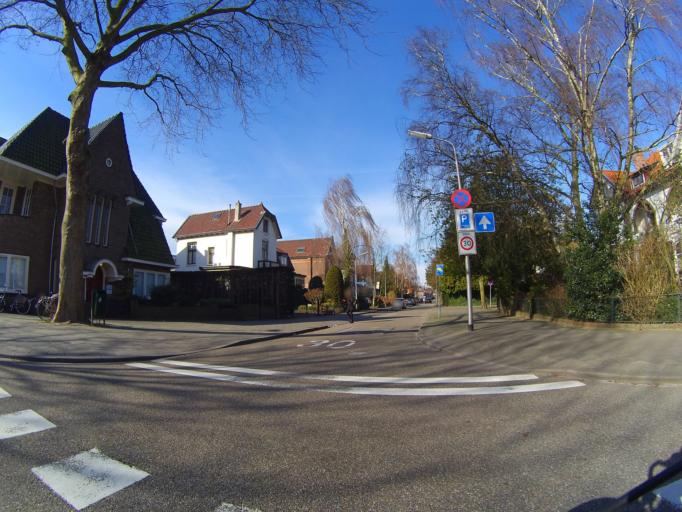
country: NL
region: North Holland
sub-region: Gemeente Bussum
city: Bussum
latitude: 52.2793
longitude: 5.1590
